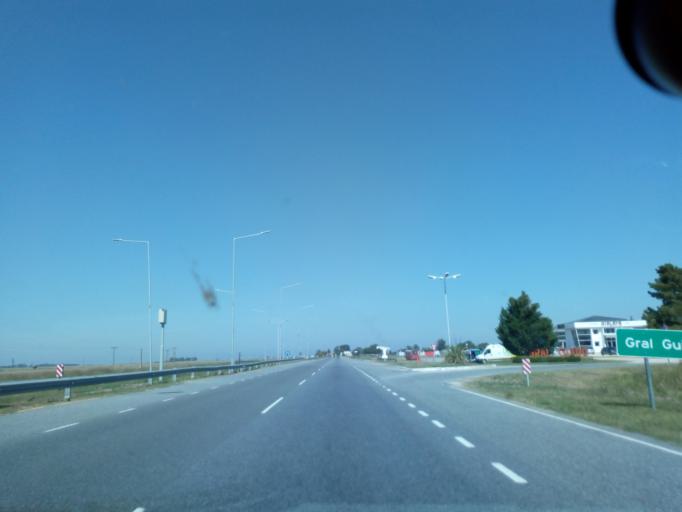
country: AR
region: Buenos Aires
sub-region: Partido de General Guido
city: General Guido
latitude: -36.6412
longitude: -57.7874
